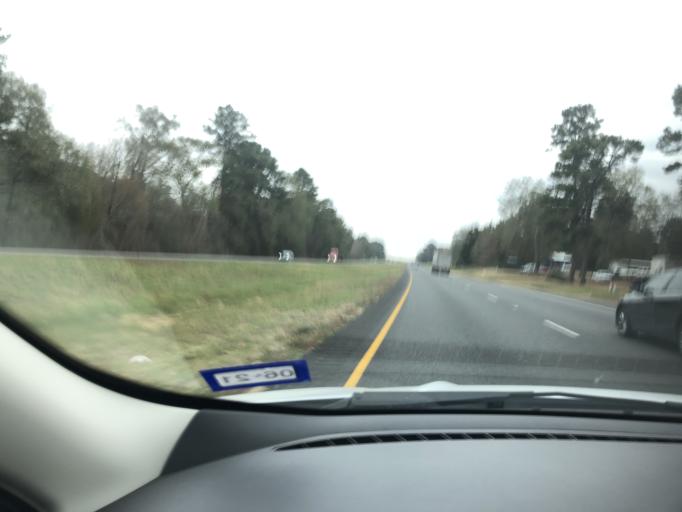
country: US
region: Texas
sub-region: Angelina County
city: Redland
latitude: 31.4743
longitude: -94.7266
